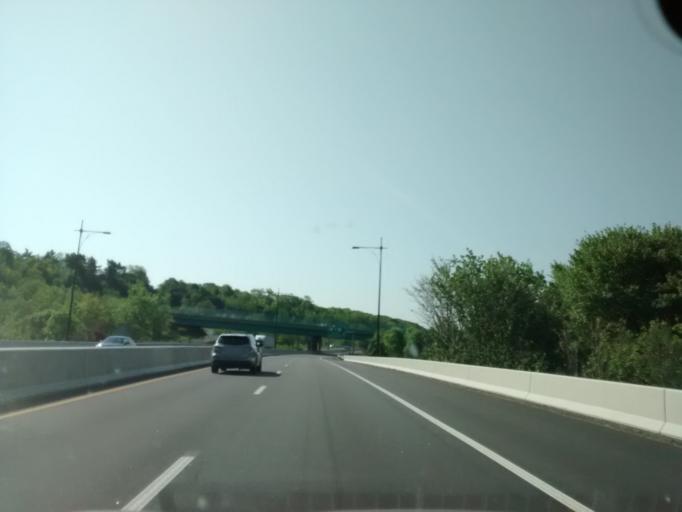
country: US
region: Massachusetts
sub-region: Worcester County
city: Sunderland
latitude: 42.2156
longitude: -71.7849
